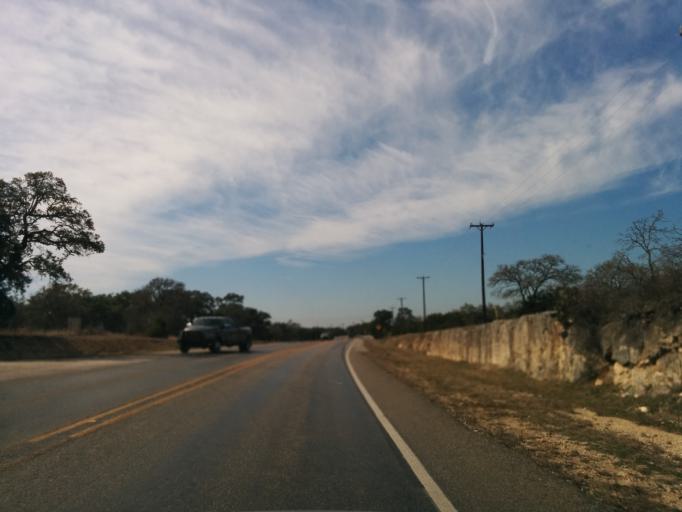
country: US
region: Texas
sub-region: Bexar County
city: Fair Oaks Ranch
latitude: 29.7566
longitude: -98.6180
